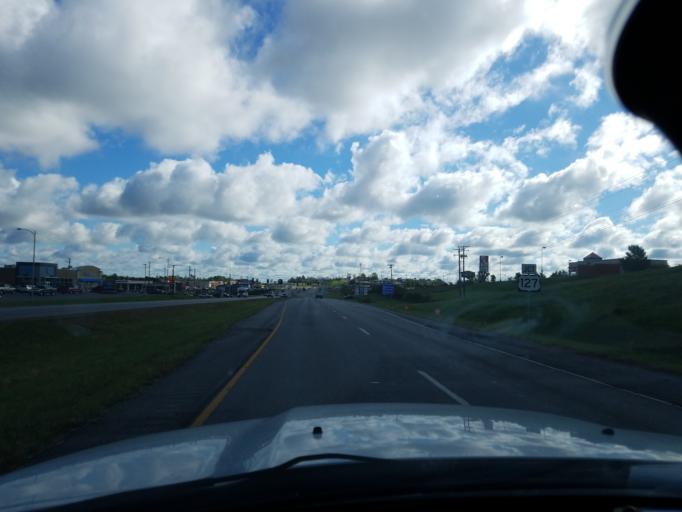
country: US
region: Kentucky
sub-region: Boyle County
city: Danville
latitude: 37.6169
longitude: -84.7798
